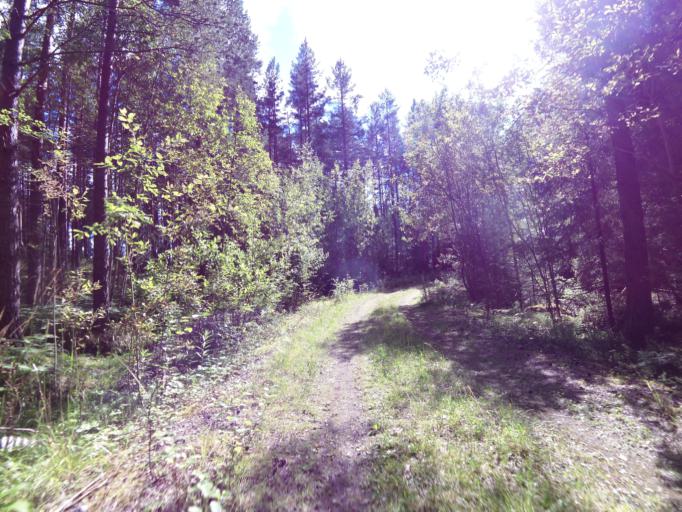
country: SE
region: Gaevleborg
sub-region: Hofors Kommun
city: Hofors
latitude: 60.5436
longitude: 16.2403
